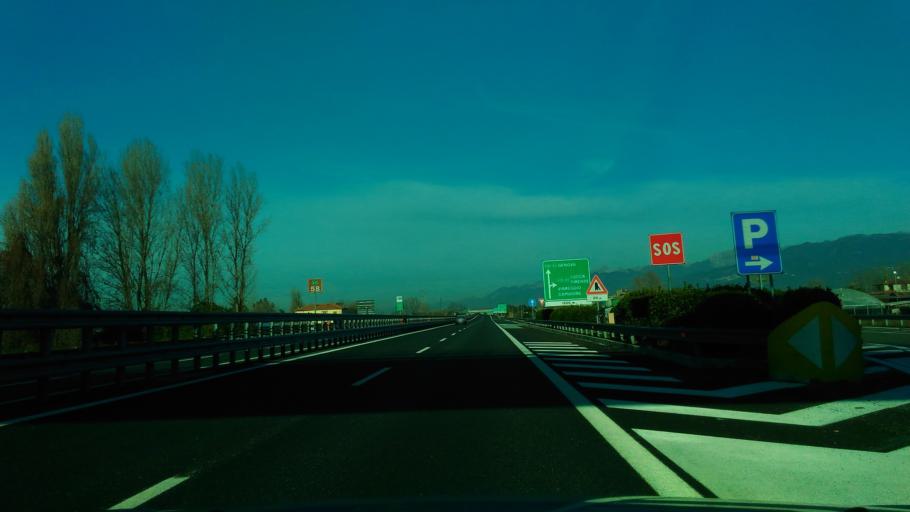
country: IT
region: Tuscany
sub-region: Provincia di Lucca
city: Viareggio
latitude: 43.8772
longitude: 10.2703
